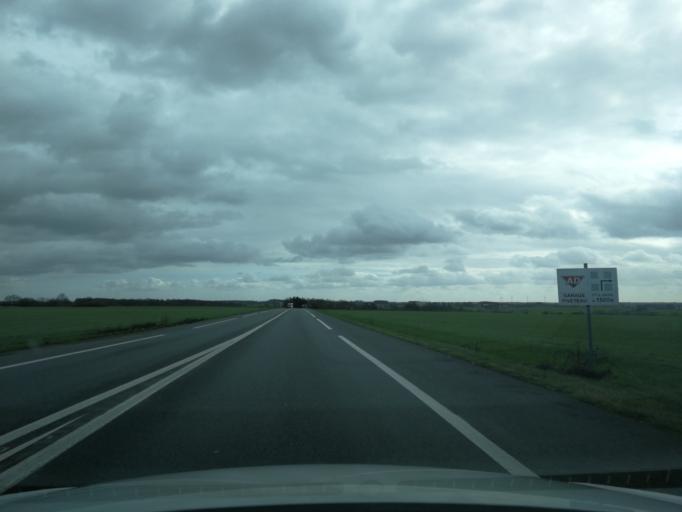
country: FR
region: Pays de la Loire
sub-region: Departement de la Vendee
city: Chavagnes-en-Paillers
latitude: 46.9123
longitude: -1.2402
